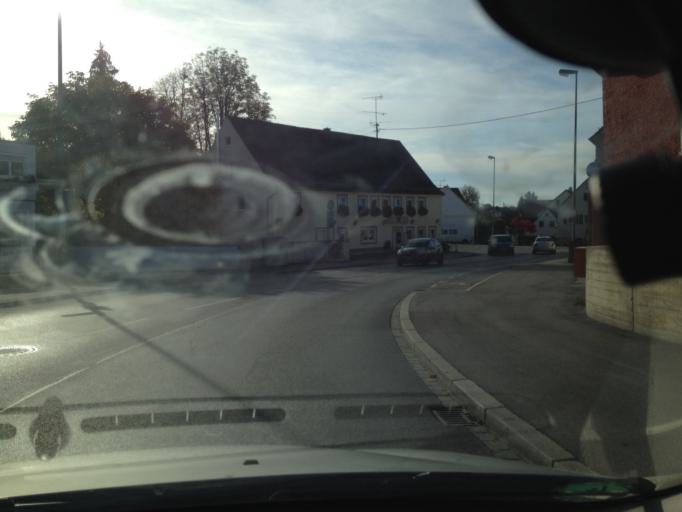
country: DE
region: Bavaria
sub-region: Swabia
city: Bobingen
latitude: 48.3141
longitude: 10.8590
